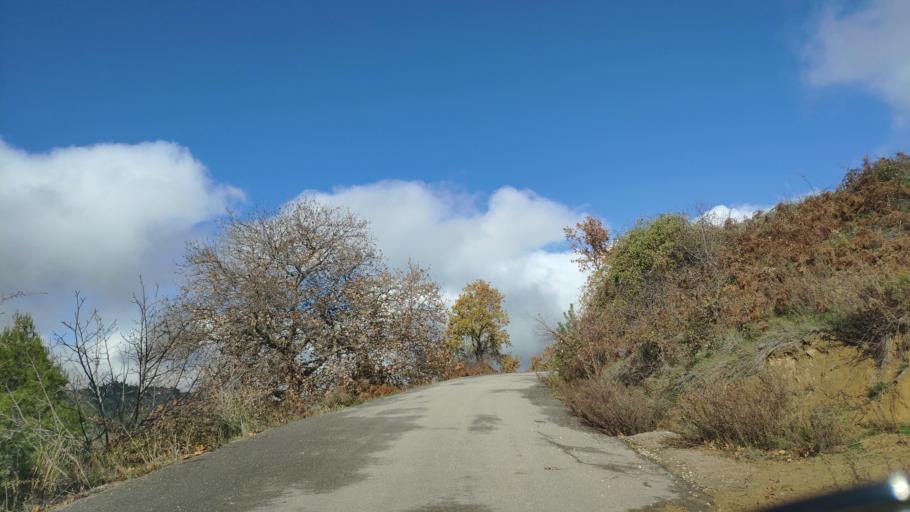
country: GR
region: West Greece
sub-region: Nomos Achaias
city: Aiyira
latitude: 38.0697
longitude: 22.4676
